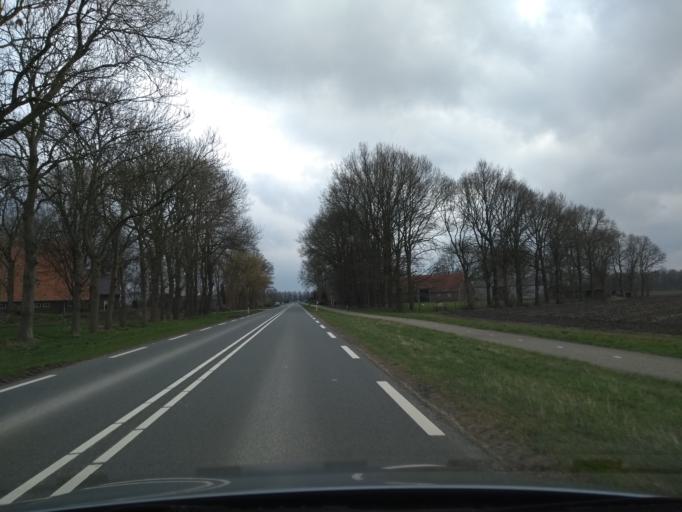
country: NL
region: Flevoland
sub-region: Gemeente Noordoostpolder
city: Ens
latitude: 52.7202
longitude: 5.8662
